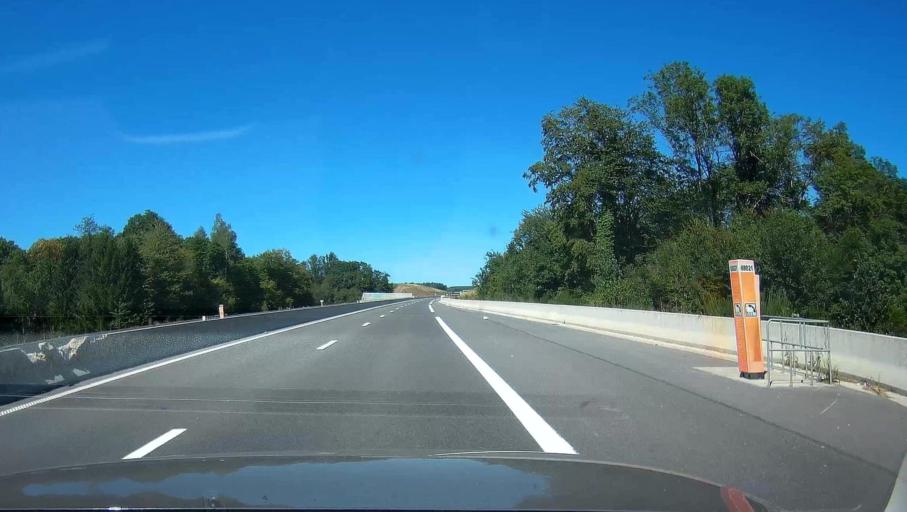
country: FR
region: Champagne-Ardenne
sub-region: Departement des Ardennes
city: Rimogne
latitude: 49.8308
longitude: 4.5116
